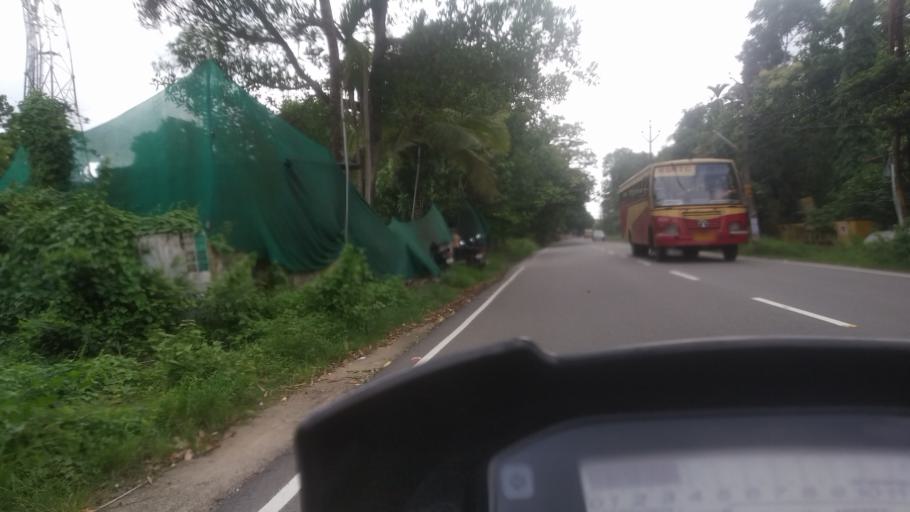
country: IN
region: Kerala
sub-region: Ernakulam
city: Elur
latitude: 10.1376
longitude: 76.2683
